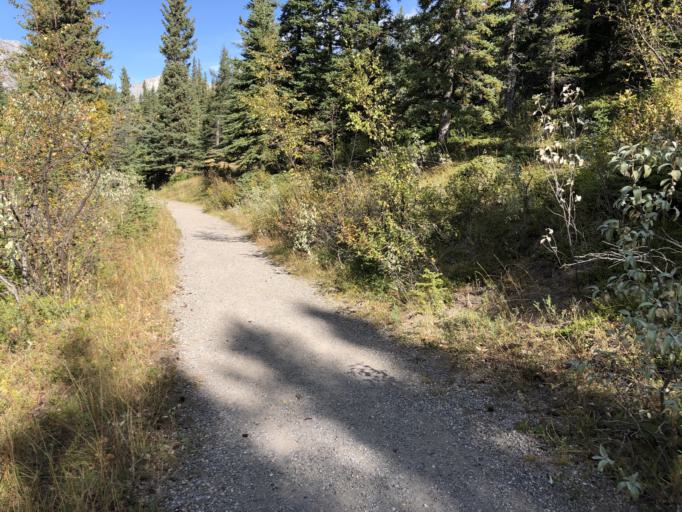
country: CA
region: Alberta
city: Canmore
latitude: 51.0723
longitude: -115.1128
